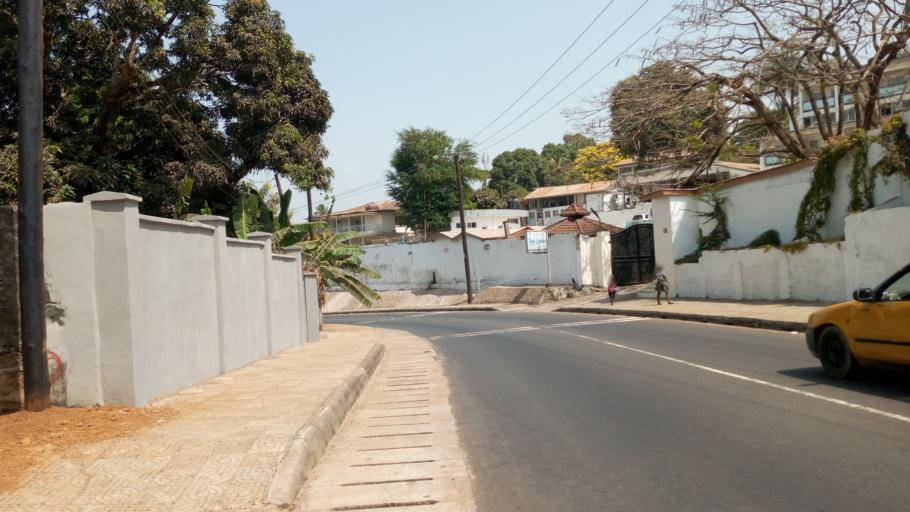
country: SL
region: Western Area
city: Freetown
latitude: 8.4827
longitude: -13.2623
